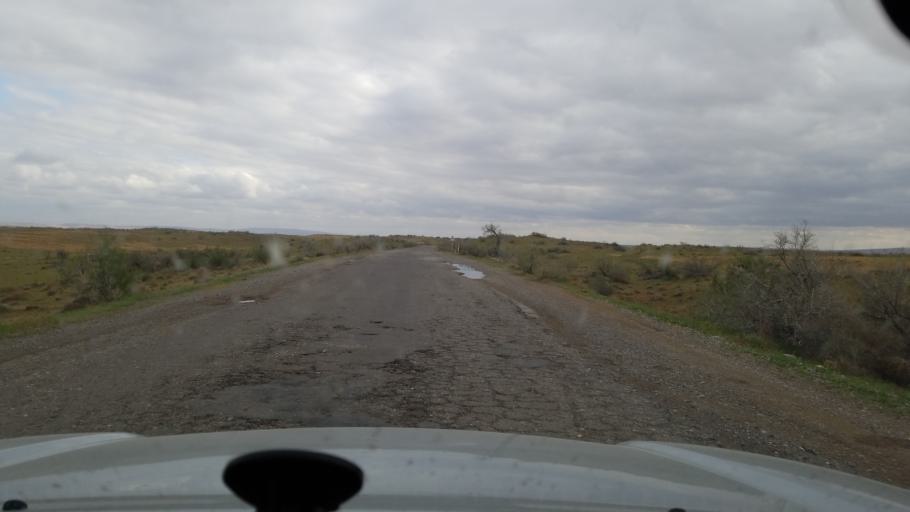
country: TM
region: Mary
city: Serhetabat
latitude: 36.0511
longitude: 62.6167
